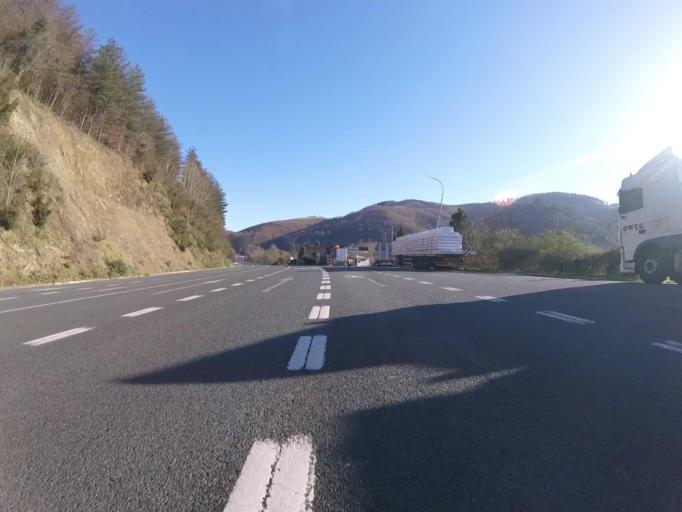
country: ES
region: Navarre
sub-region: Provincia de Navarra
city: Bera
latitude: 43.2789
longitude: -1.7108
